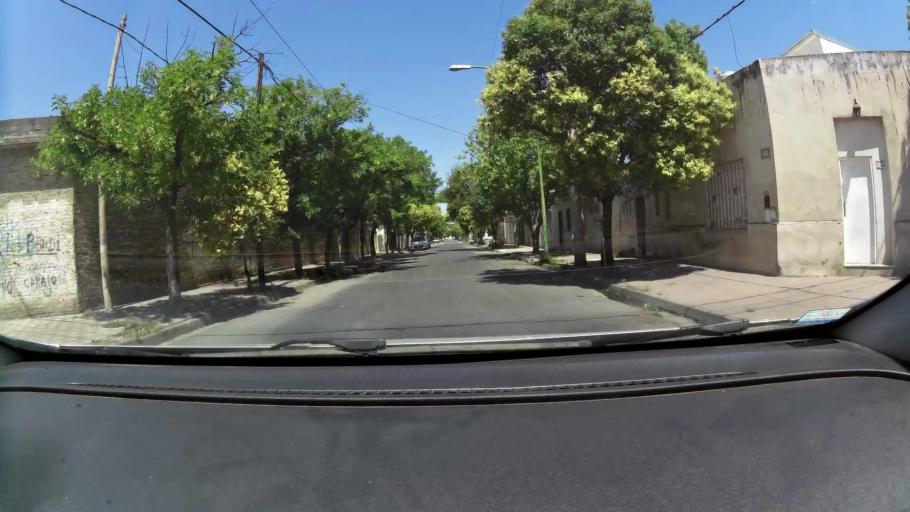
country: AR
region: Cordoba
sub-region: Departamento de Capital
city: Cordoba
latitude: -31.3886
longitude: -64.1521
